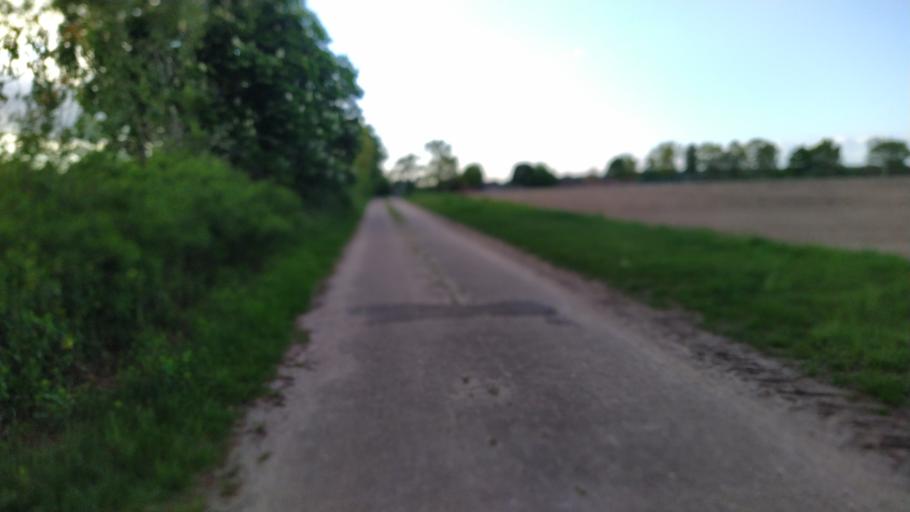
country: DE
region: Lower Saxony
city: Farven
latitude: 53.4346
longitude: 9.3288
